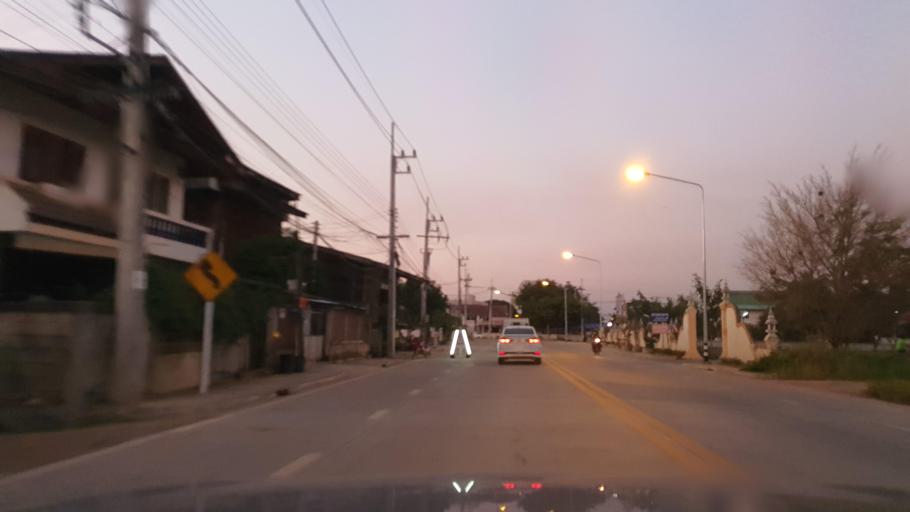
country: TH
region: Phayao
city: Dok Kham Tai
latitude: 19.1603
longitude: 99.9931
